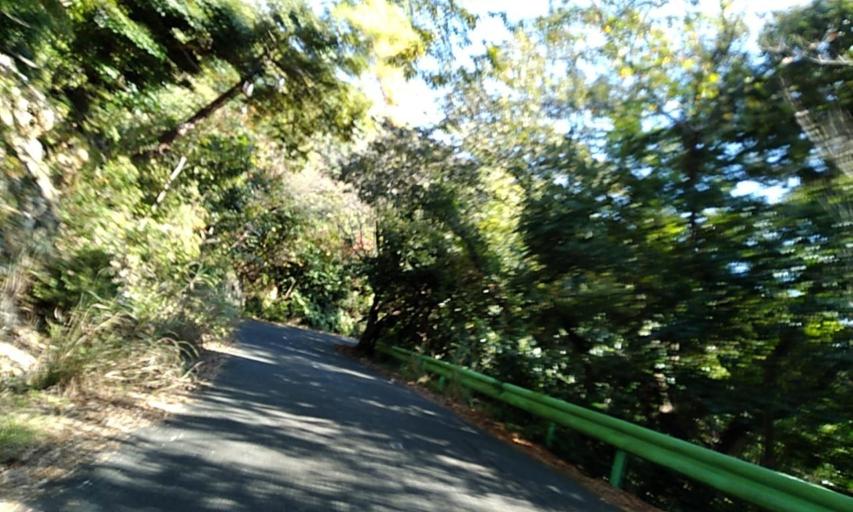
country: JP
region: Shizuoka
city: Hamakita
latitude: 34.8174
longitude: 137.6429
